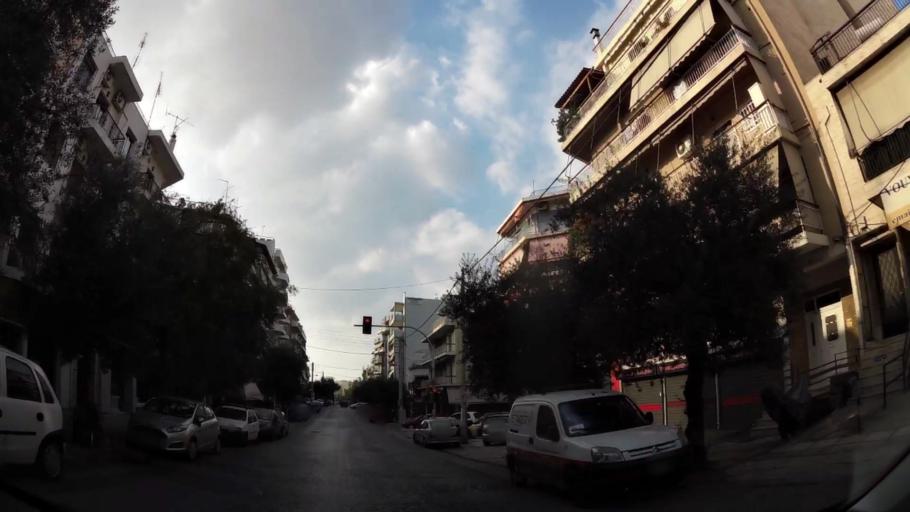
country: GR
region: Attica
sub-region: Nomarchia Athinas
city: Dhafni
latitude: 37.9530
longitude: 23.7258
